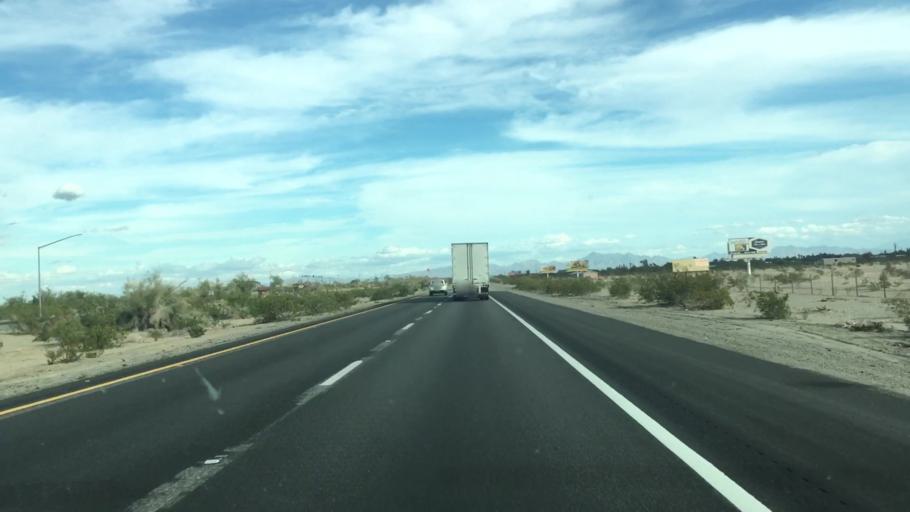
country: US
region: California
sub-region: Riverside County
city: Mesa Verde
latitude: 33.6089
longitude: -114.7461
